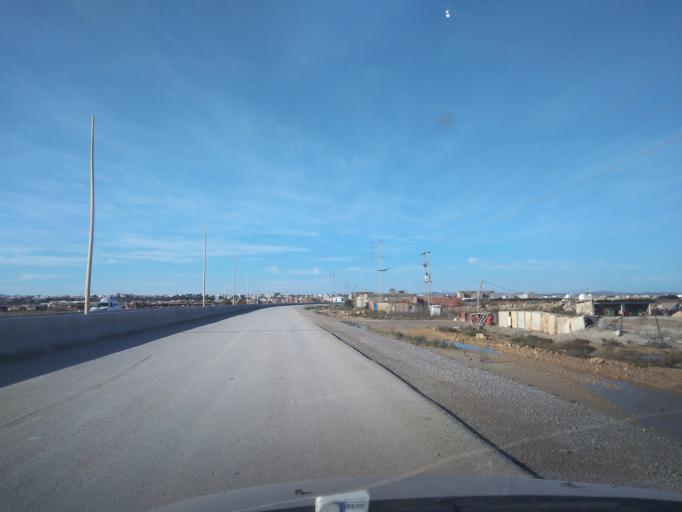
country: TN
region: Ariana
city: Qal'at al Andalus
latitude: 37.0456
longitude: 10.1265
